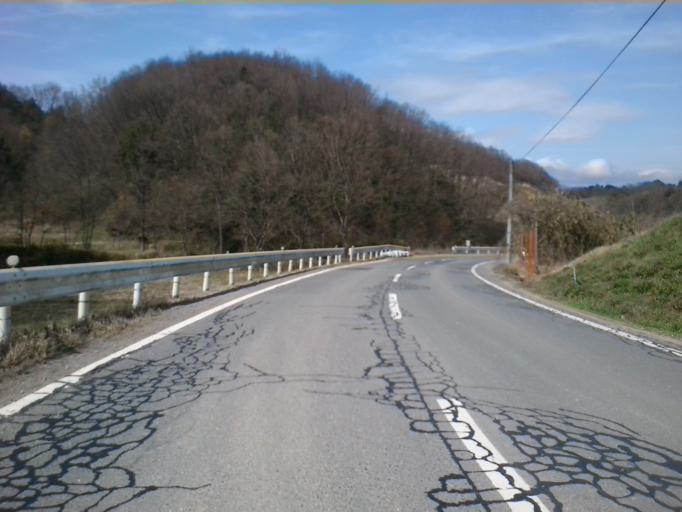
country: JP
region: Nara
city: Nara-shi
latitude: 34.7128
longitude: 135.8876
